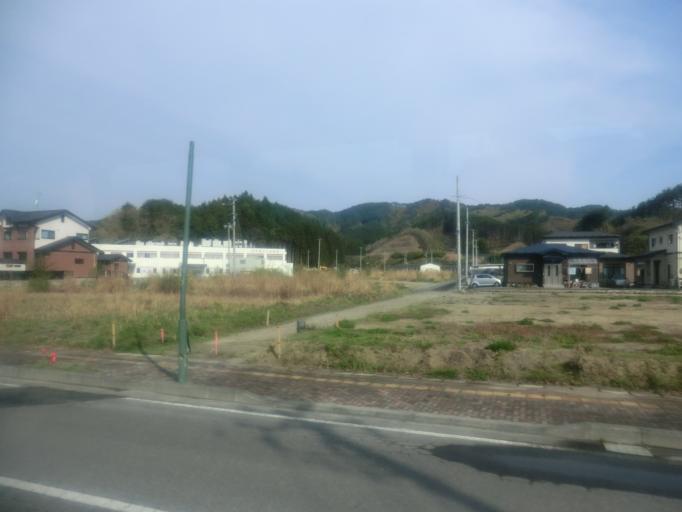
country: JP
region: Iwate
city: Yamada
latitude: 39.4777
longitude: 141.9551
